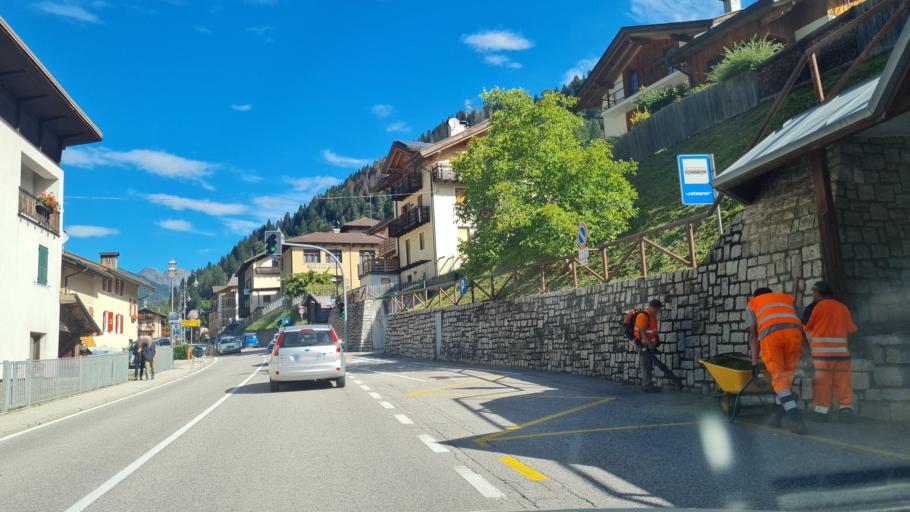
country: IT
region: Trentino-Alto Adige
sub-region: Provincia di Trento
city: Siror
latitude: 46.1870
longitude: 11.8305
